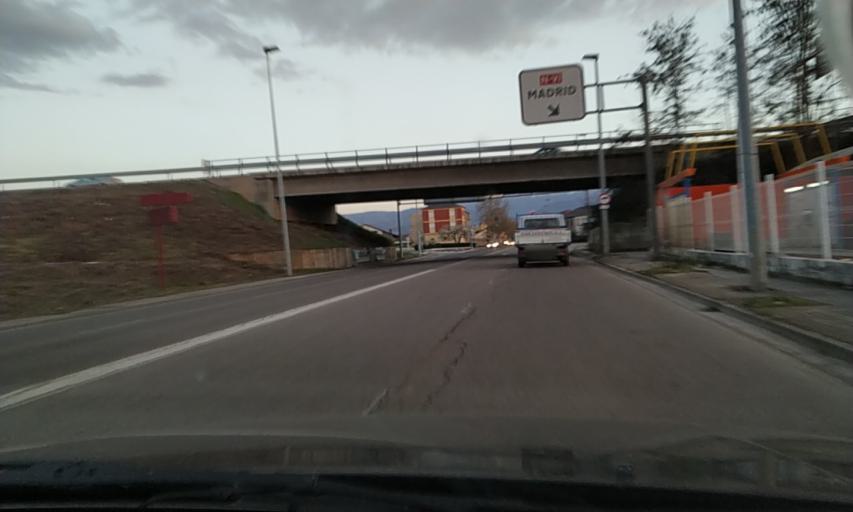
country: ES
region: Castille and Leon
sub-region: Provincia de Leon
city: Ponferrada
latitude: 42.5691
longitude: -6.6072
